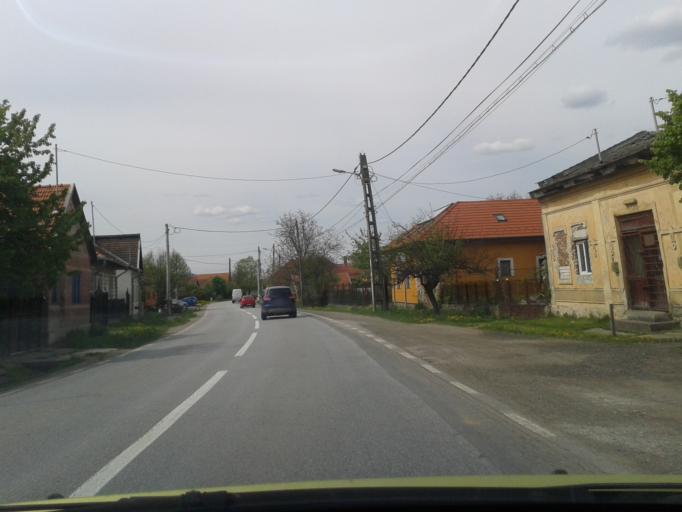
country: RO
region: Hunedoara
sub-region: Comuna Dobra
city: Dobra
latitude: 45.9151
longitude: 22.5640
